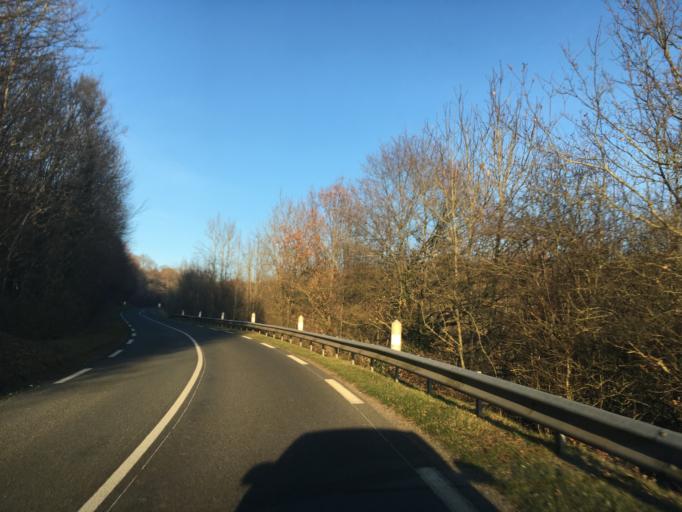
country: FR
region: Haute-Normandie
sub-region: Departement de l'Eure
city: Houlbec-Cocherel
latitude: 49.0546
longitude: 1.3462
